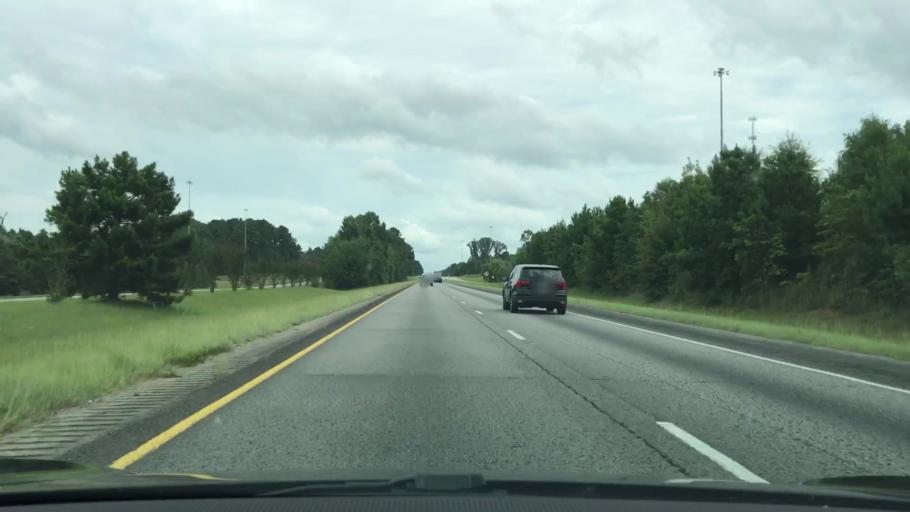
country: US
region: Georgia
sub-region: Troup County
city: West Point
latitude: 32.9298
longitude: -85.1079
